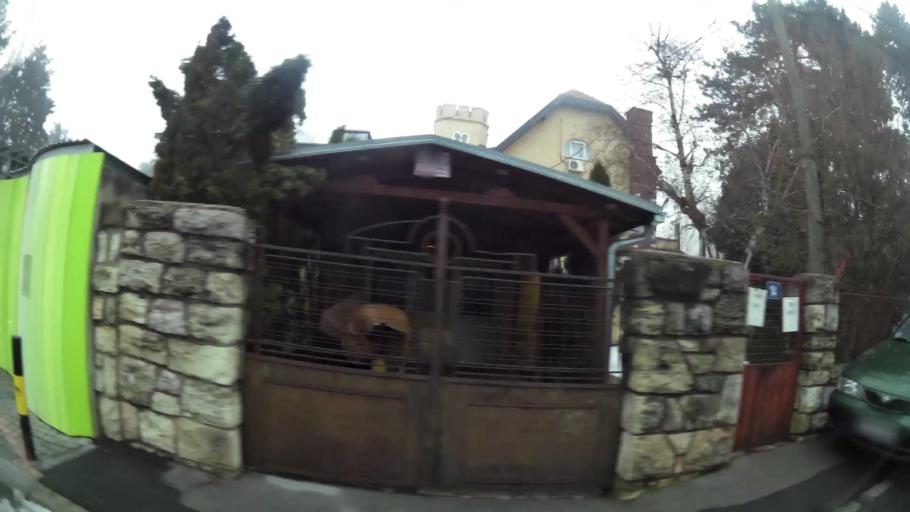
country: RS
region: Central Serbia
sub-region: Belgrade
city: Cukarica
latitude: 44.7900
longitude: 20.4349
